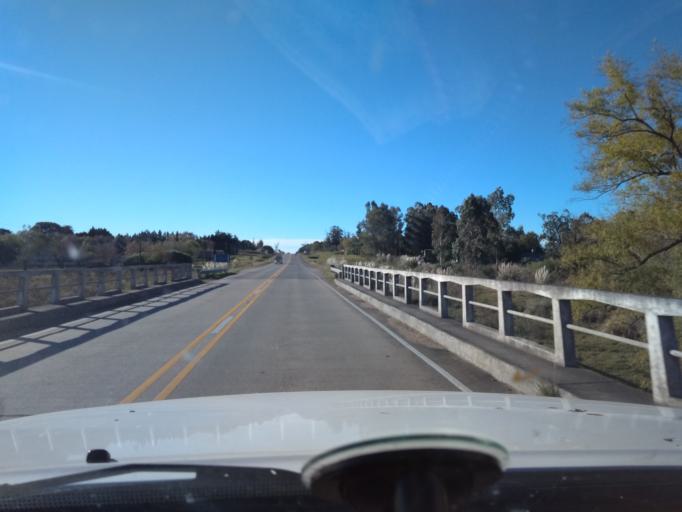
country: UY
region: Canelones
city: Sauce
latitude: -34.6156
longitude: -56.0493
